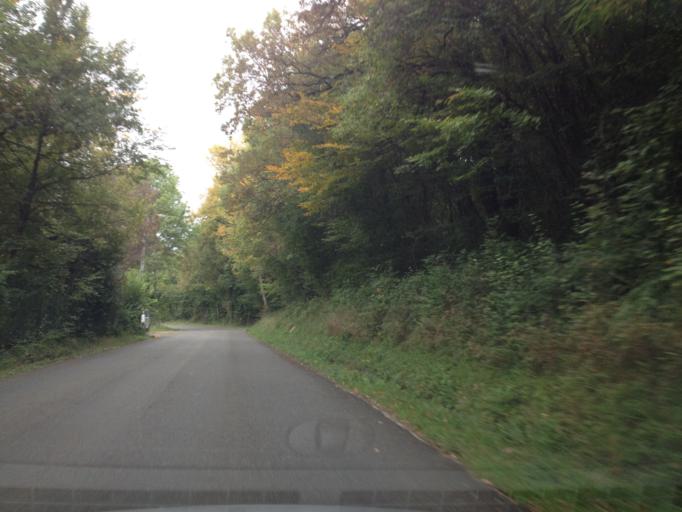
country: FR
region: Rhone-Alpes
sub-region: Departement de la Savoie
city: Mouxy
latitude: 45.6954
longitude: 5.9394
